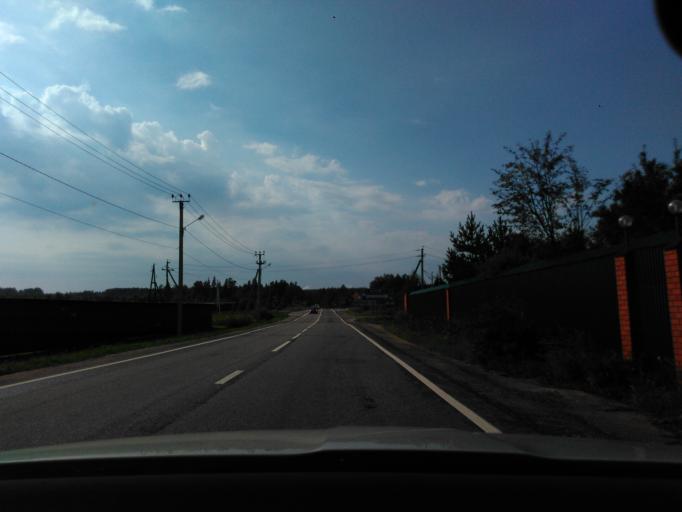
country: RU
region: Moskovskaya
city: Solnechnogorsk
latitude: 56.1395
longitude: 36.8420
